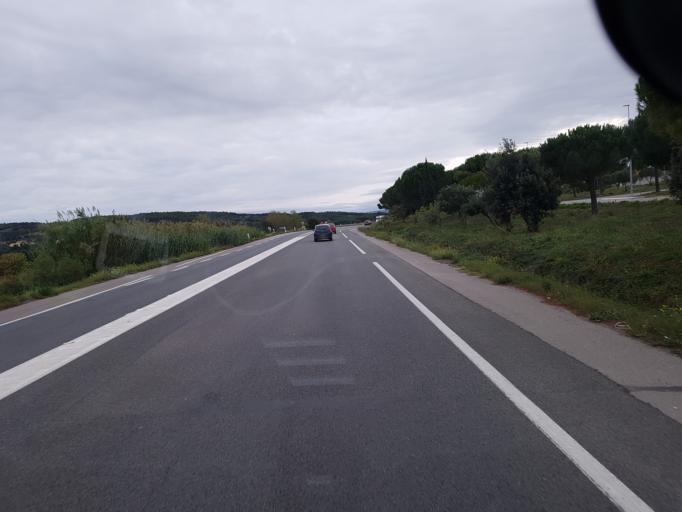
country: FR
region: Languedoc-Roussillon
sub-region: Departement de l'Aude
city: Narbonne
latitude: 43.1407
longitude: 2.9730
